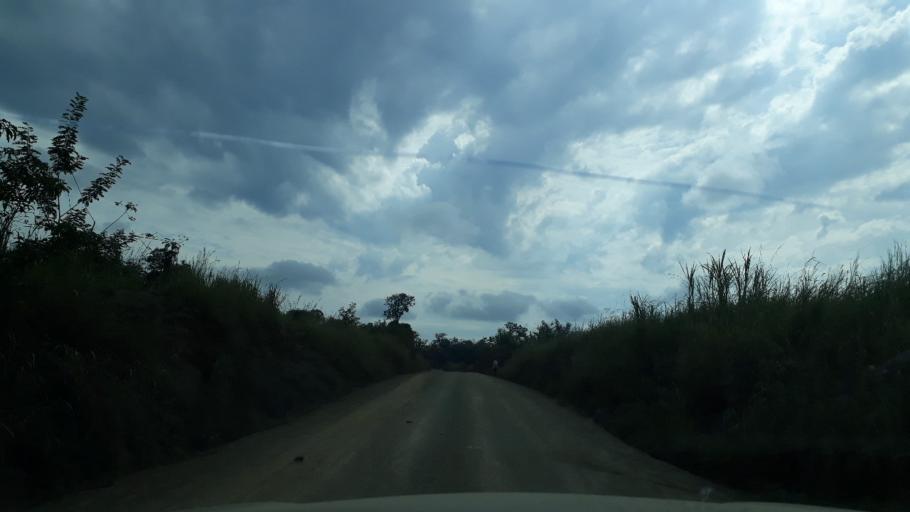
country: CD
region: Eastern Province
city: Bunia
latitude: 1.4436
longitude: 29.8528
